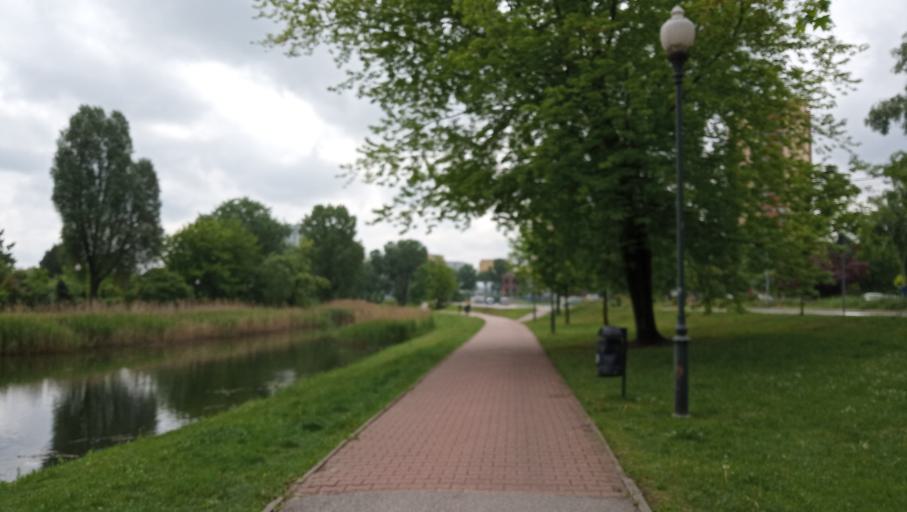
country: PL
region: Masovian Voivodeship
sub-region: Warszawa
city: Zoliborz
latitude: 52.2851
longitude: 20.9793
